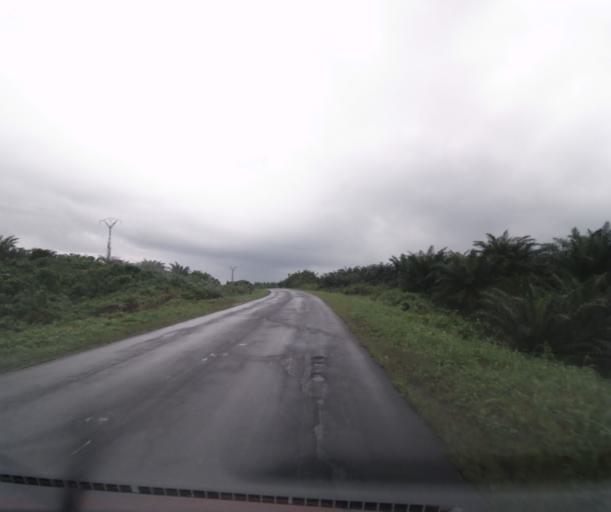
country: CM
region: South-West Province
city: Idenao
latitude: 4.1517
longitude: 8.9903
